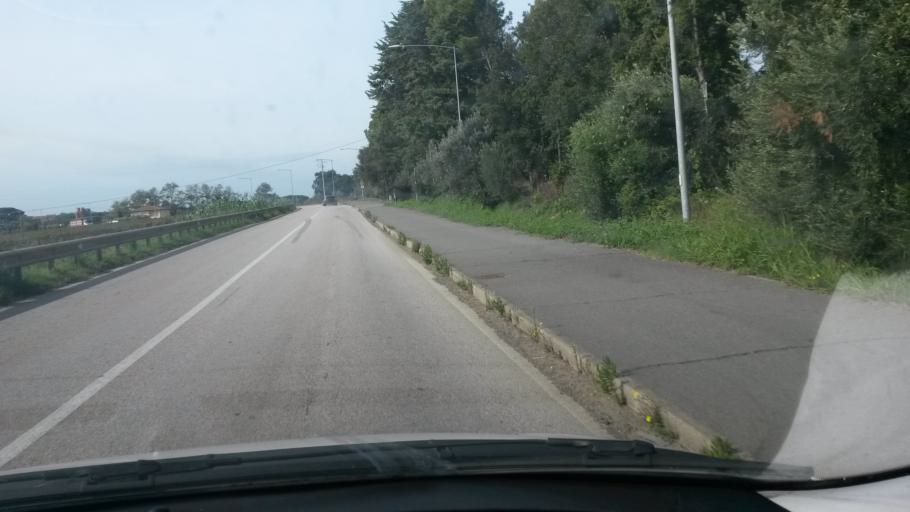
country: IT
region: Tuscany
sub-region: Provincia di Livorno
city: S.P. in Palazzi
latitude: 43.3340
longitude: 10.5173
